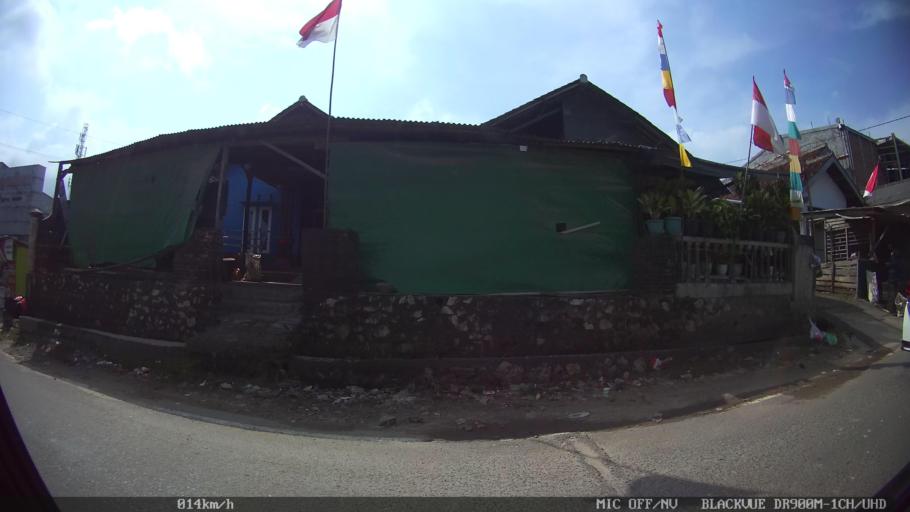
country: ID
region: Lampung
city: Kedaton
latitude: -5.3576
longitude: 105.2607
